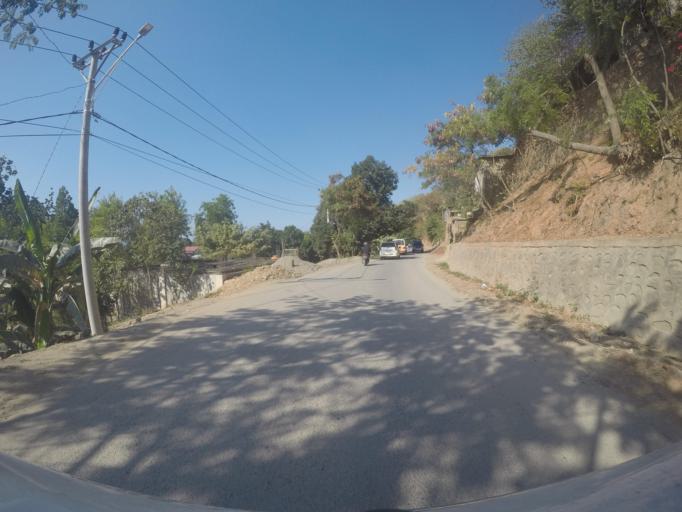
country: TL
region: Dili
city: Dili
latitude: -8.5689
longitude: 125.5457
